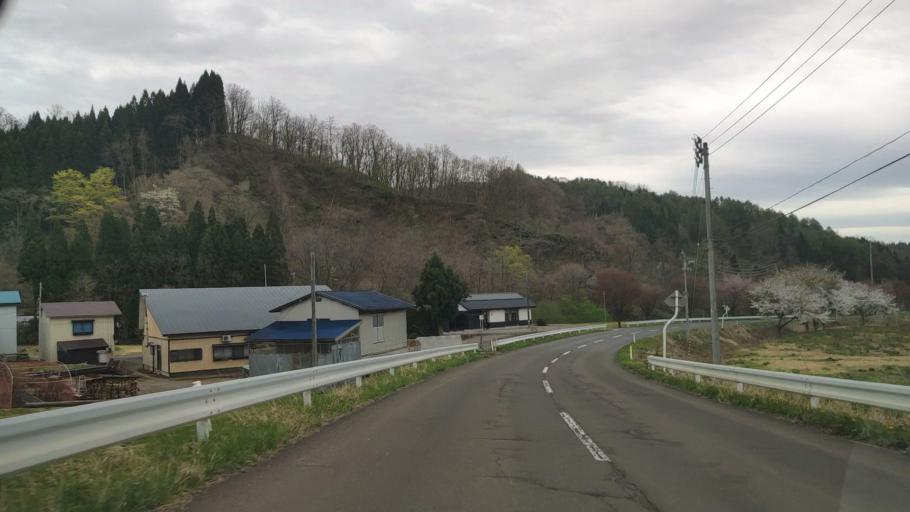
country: JP
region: Akita
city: Hanawa
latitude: 40.3597
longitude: 140.7852
